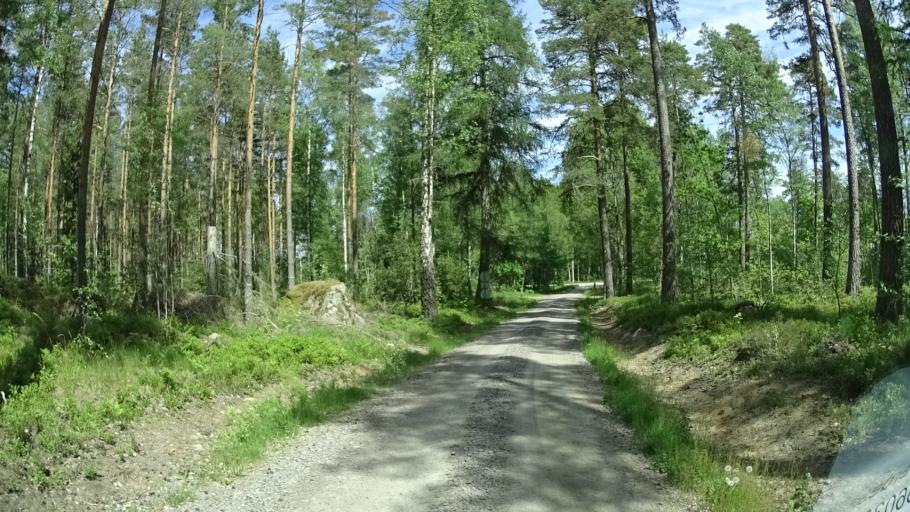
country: SE
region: OEstergoetland
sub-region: Norrkopings Kommun
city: Svartinge
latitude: 58.7717
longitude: 15.9665
